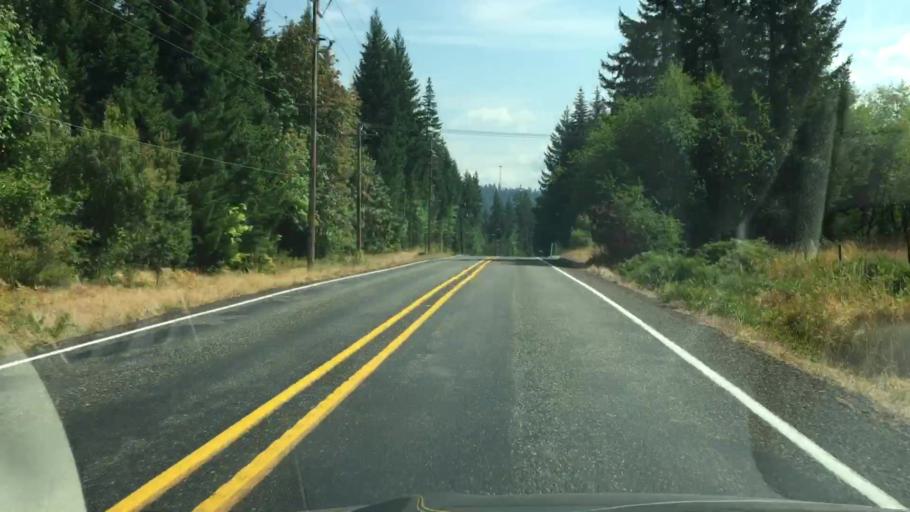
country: US
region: Washington
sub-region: Klickitat County
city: White Salmon
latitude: 45.8695
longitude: -121.5136
